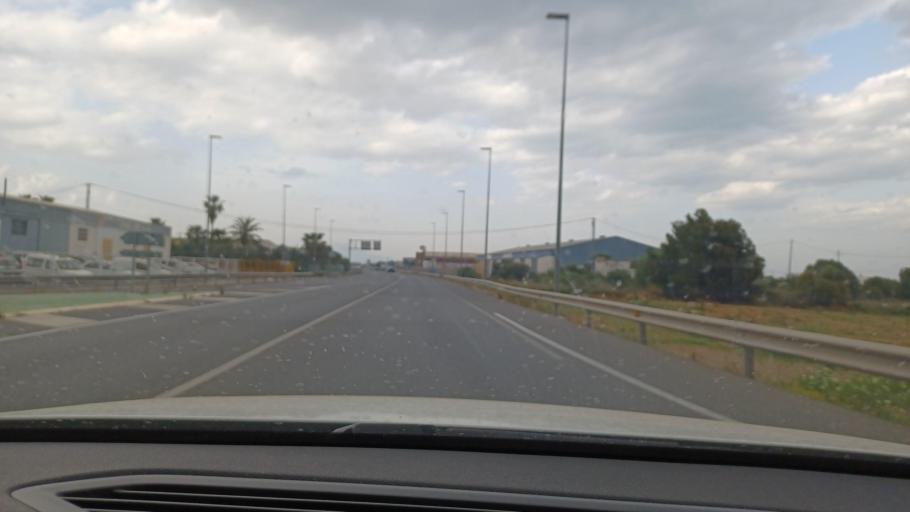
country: ES
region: Valencia
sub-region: Provincia de Castello
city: Benicarlo
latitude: 40.4323
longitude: 0.4376
